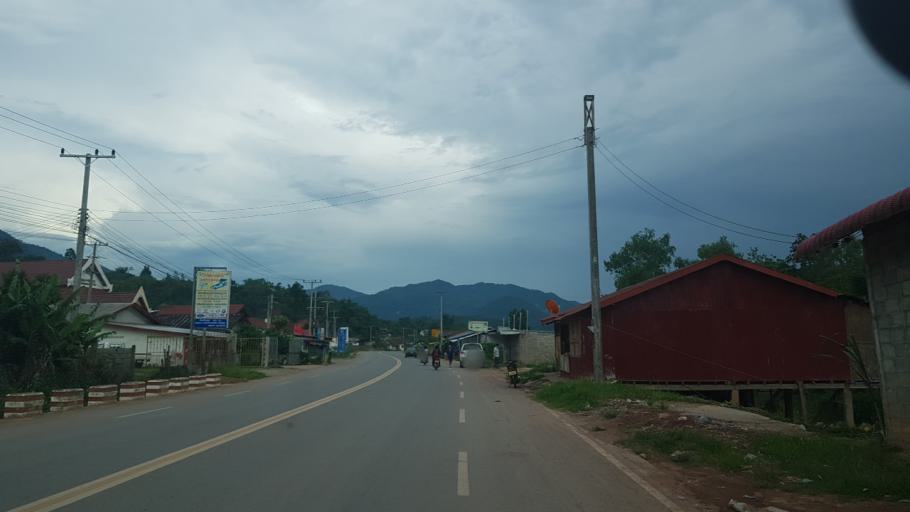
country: LA
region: Oudomxai
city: Muang Xay
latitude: 20.6572
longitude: 101.9767
